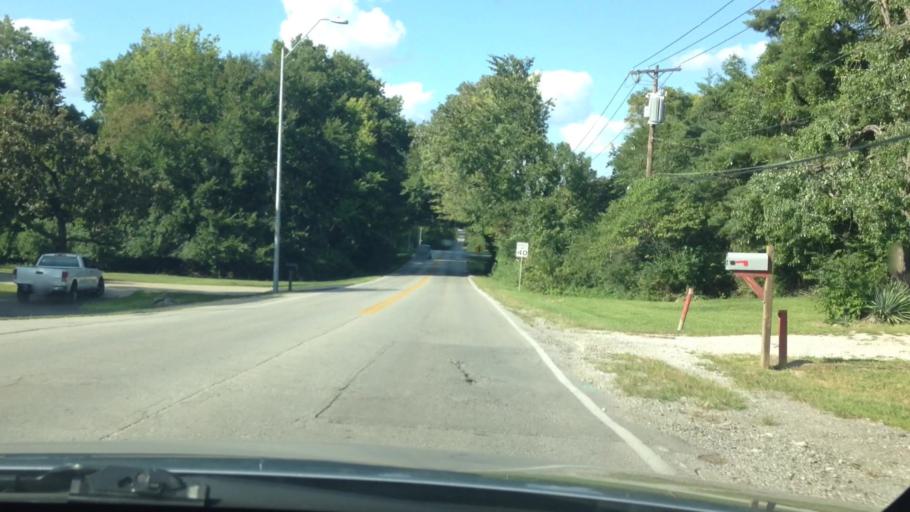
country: US
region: Missouri
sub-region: Jackson County
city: Grandview
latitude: 38.9034
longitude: -94.5850
